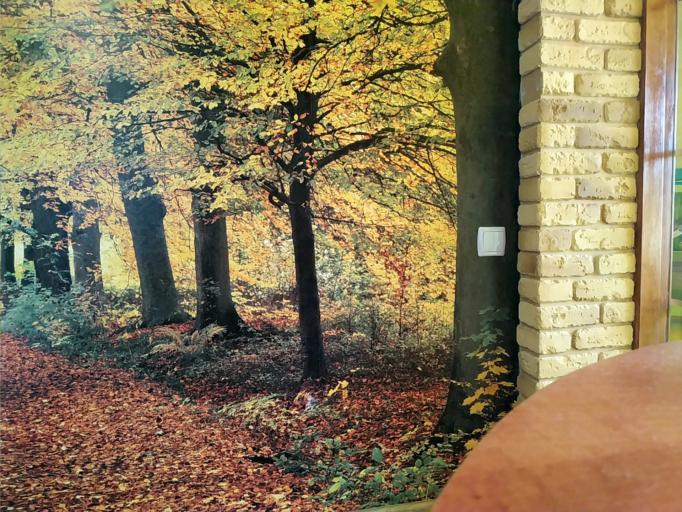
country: RU
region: Novgorod
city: Sol'tsy
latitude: 57.9044
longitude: 30.2217
